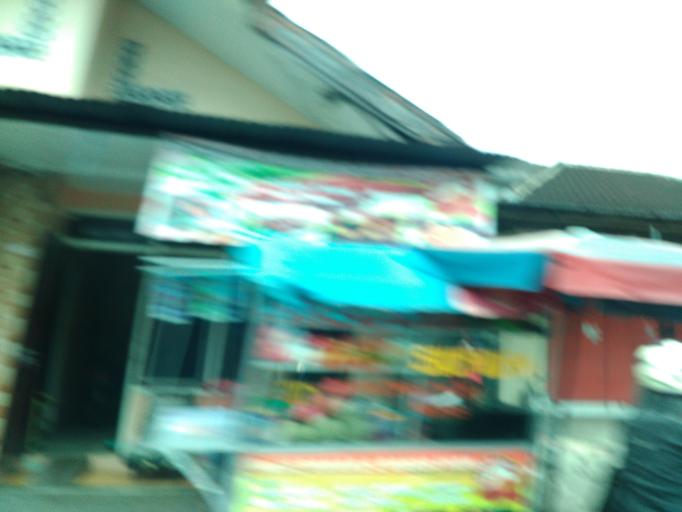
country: ID
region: Central Java
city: Delanggu
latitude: -7.6231
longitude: 110.7058
